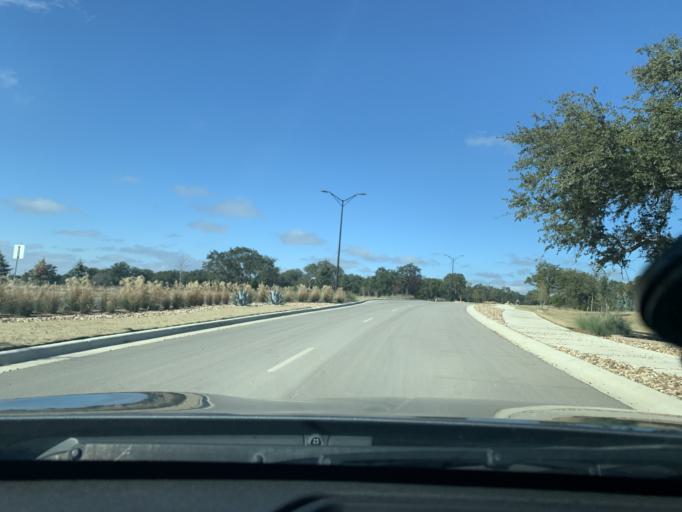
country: US
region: Texas
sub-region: Williamson County
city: Serenada
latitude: 30.7320
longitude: -97.7607
